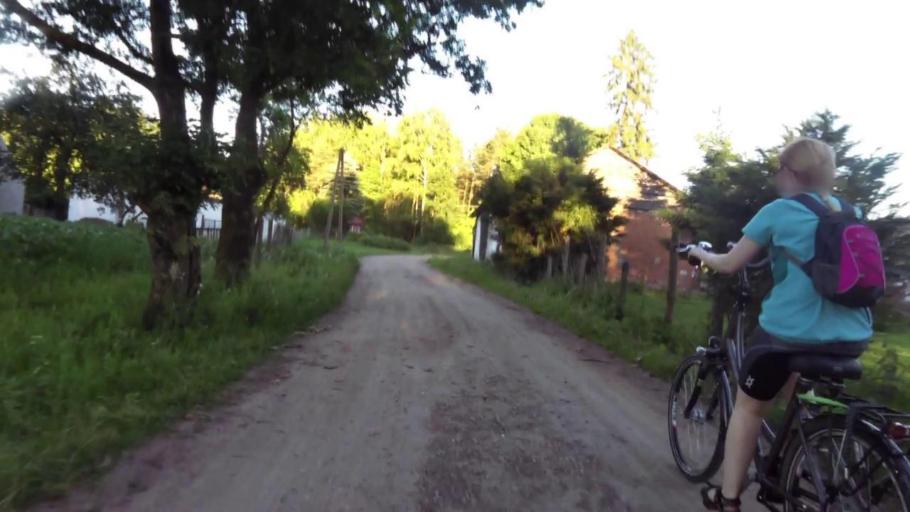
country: PL
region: West Pomeranian Voivodeship
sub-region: Powiat bialogardzki
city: Bialogard
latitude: 54.0618
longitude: 16.1112
